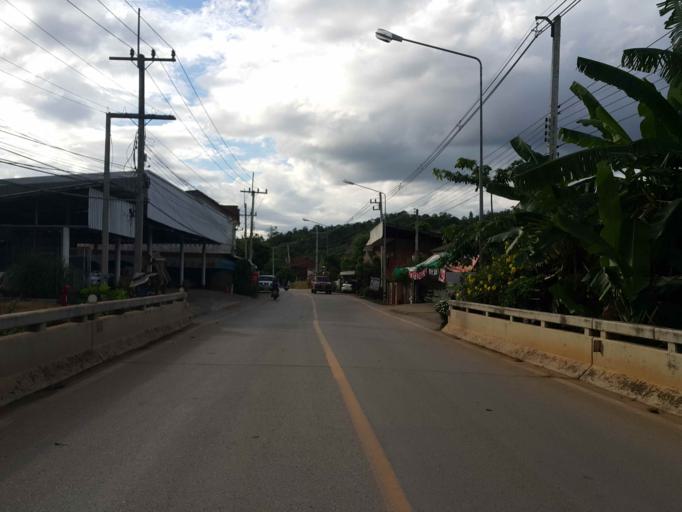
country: TH
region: Chiang Mai
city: Mae Chaem
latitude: 18.4912
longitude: 98.3770
